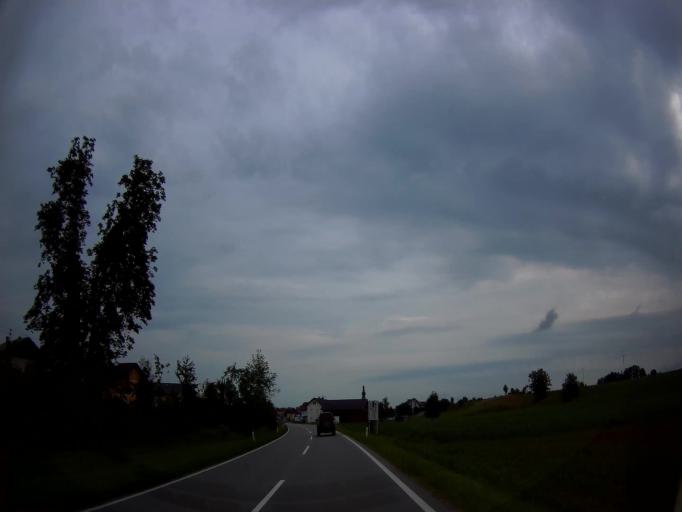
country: AT
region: Upper Austria
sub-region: Politischer Bezirk Braunau am Inn
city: Altheim
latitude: 48.2293
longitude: 13.1744
